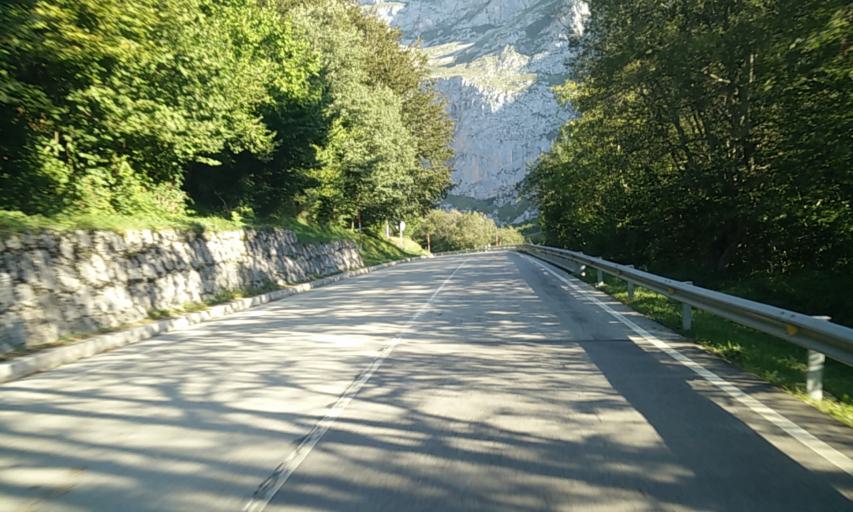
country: ES
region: Castille and Leon
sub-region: Provincia de Leon
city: Posada de Valdeon
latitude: 43.1416
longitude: -4.8100
